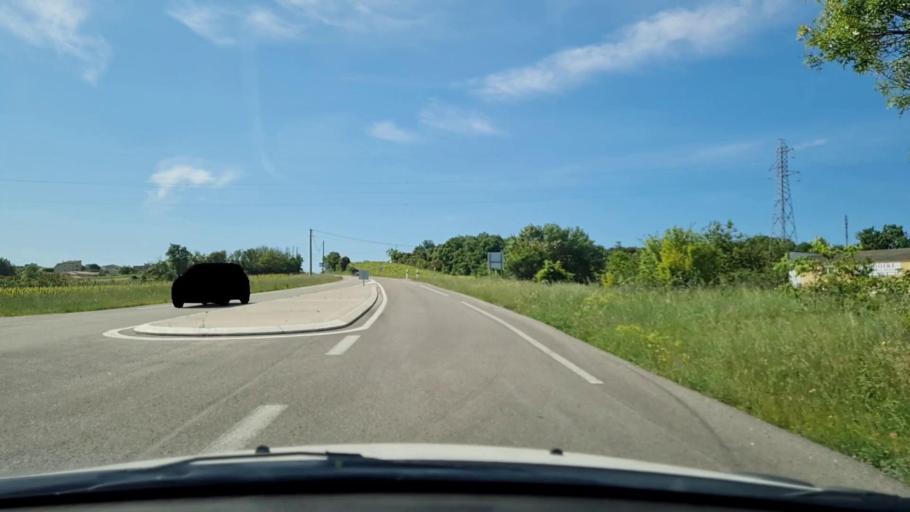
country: FR
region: Languedoc-Roussillon
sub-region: Departement du Gard
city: Vezenobres
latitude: 44.0304
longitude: 4.1509
